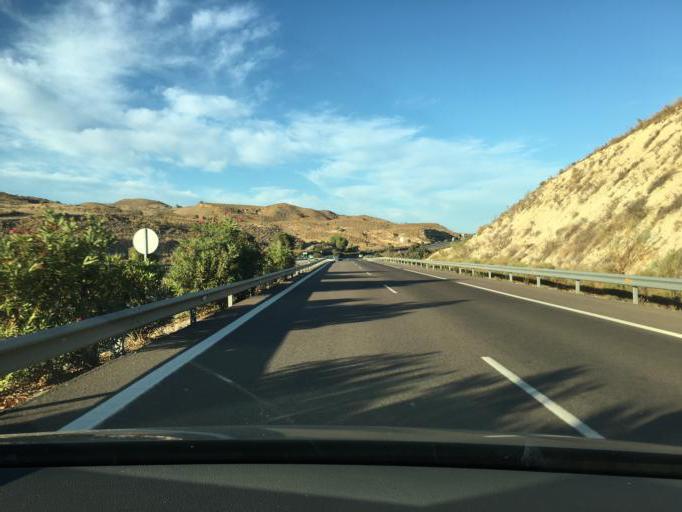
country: ES
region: Andalusia
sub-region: Provincia de Almeria
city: Bedar
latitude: 37.1338
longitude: -2.0080
